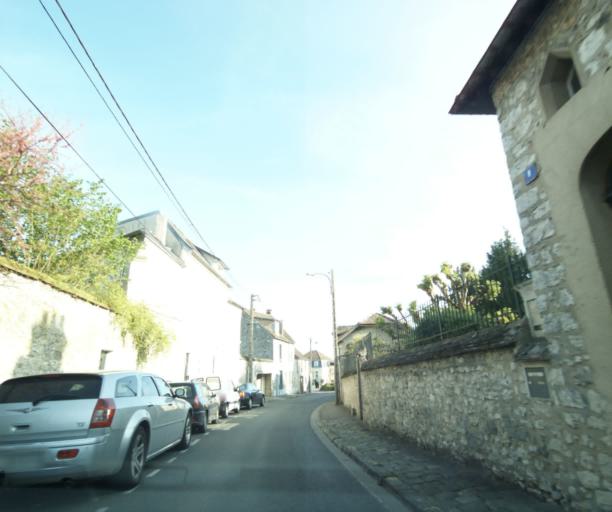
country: FR
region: Ile-de-France
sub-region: Departement de Seine-et-Marne
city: Moret-sur-Loing
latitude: 48.3727
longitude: 2.8146
